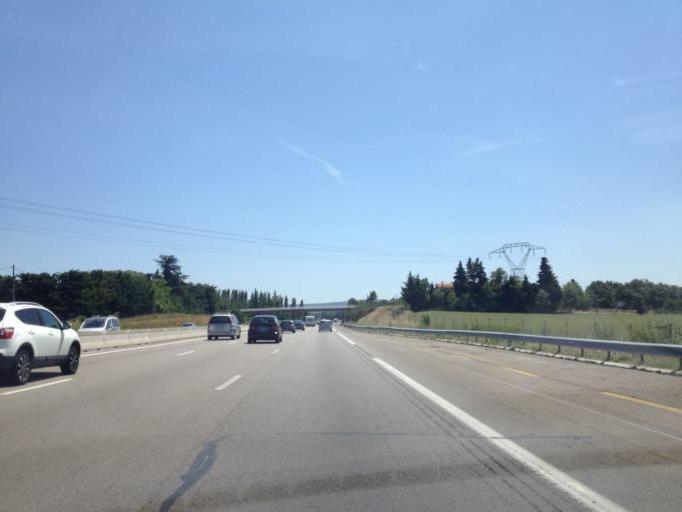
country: FR
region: Rhone-Alpes
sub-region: Departement de la Drome
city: Saint-Marcel-les-Sauzet
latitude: 44.5731
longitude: 4.8082
